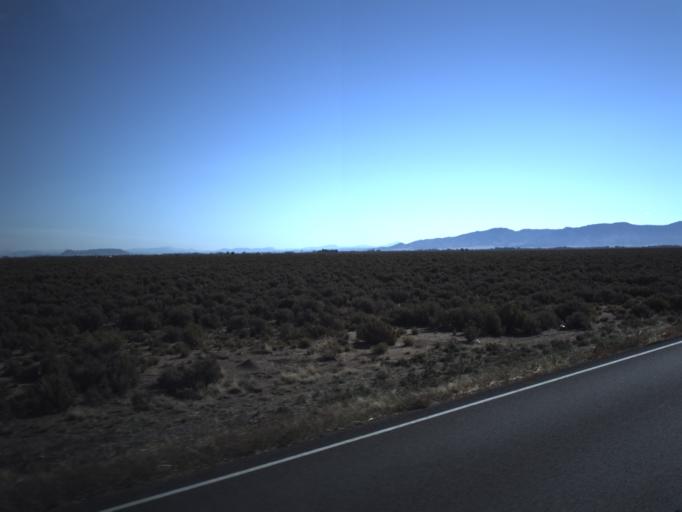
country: US
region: Utah
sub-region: Washington County
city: Enterprise
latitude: 37.7416
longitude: -113.7458
